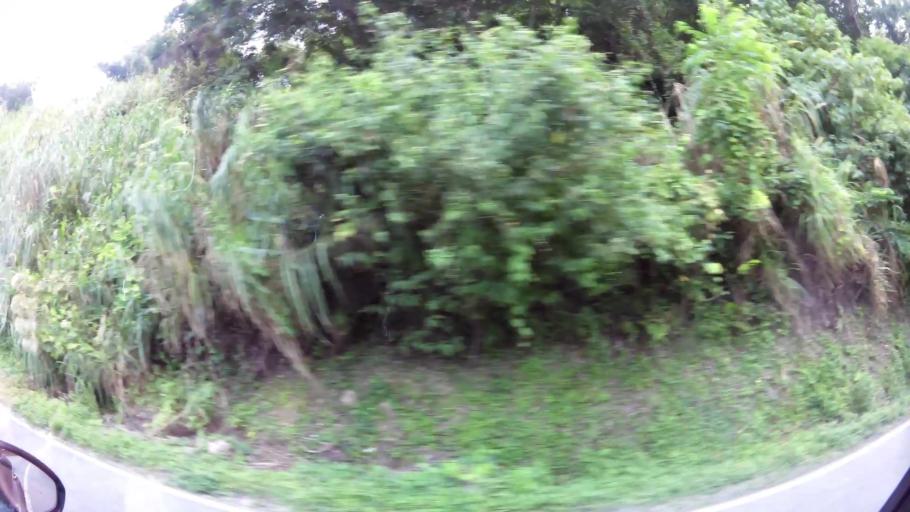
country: TT
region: Diego Martin
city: Petit Valley
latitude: 10.7278
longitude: -61.4941
